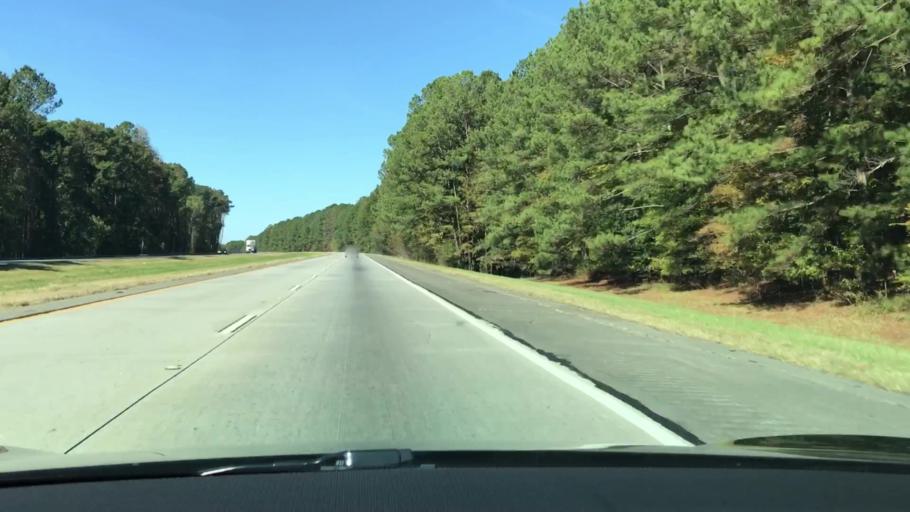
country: US
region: Georgia
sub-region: Taliaferro County
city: Crawfordville
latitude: 33.5225
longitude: -82.8719
